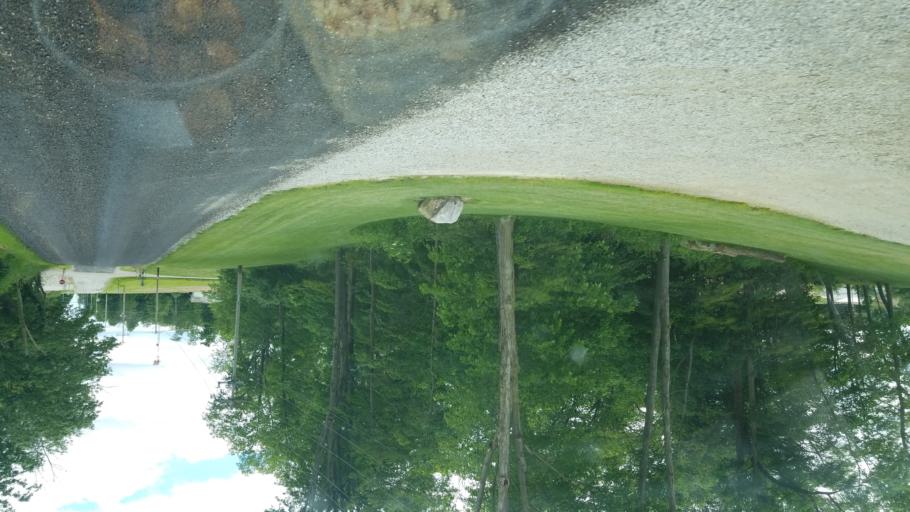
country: US
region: Ohio
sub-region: Crawford County
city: Galion
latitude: 40.6529
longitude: -82.7168
